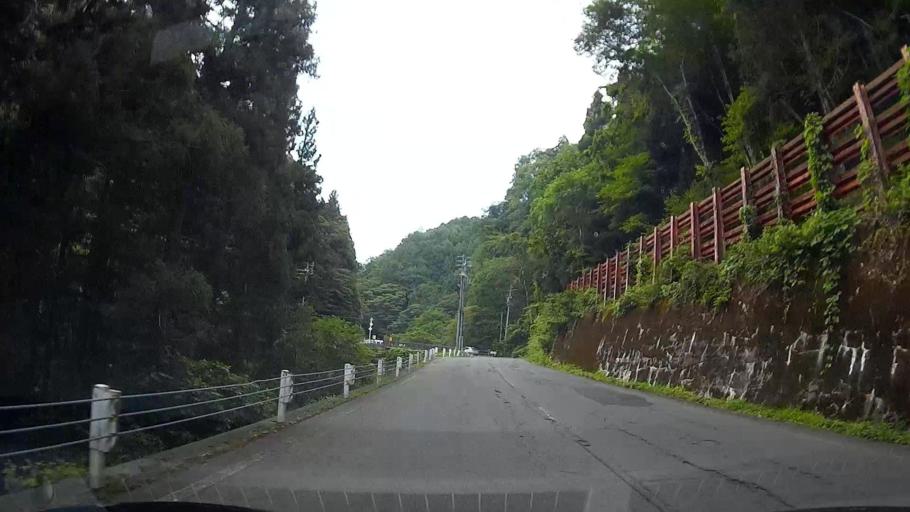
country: JP
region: Nagano
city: Iiyama
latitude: 36.8259
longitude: 138.4254
